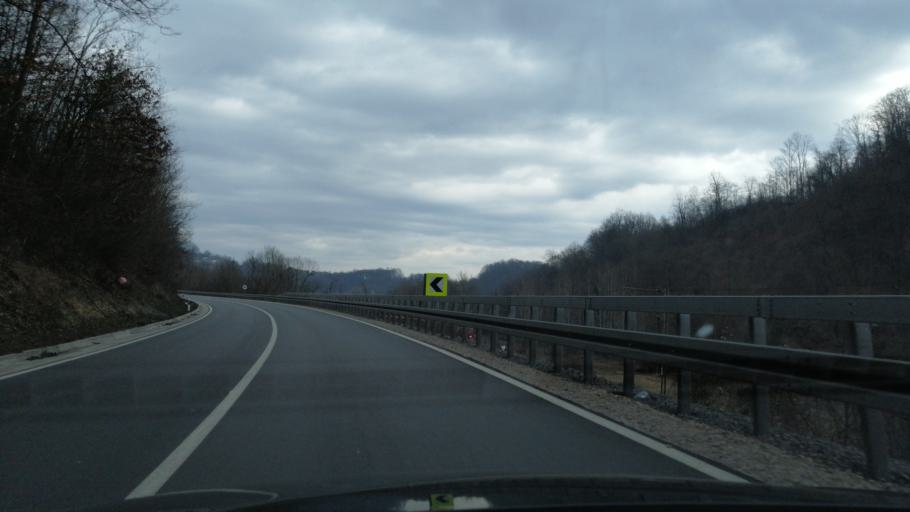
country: RS
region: Central Serbia
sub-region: Zlatiborski Okrug
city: Pozega
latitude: 43.8101
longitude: 19.9954
